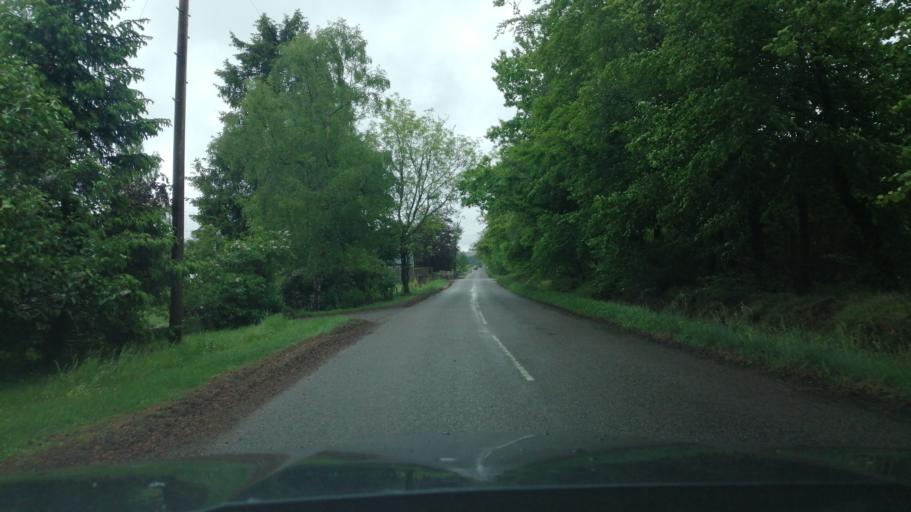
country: GB
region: Scotland
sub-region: Aberdeenshire
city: Huntly
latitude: 57.5422
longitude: -2.7929
